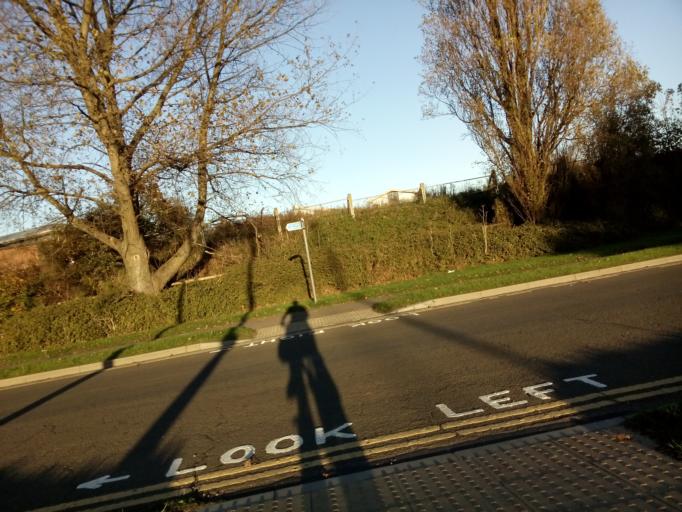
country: GB
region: England
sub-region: Suffolk
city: Felixstowe
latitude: 51.9558
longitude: 1.3279
